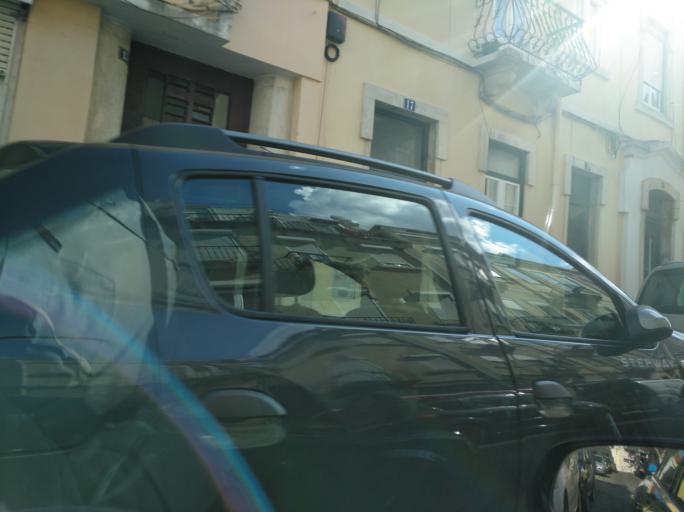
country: PT
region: Lisbon
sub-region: Lisbon
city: Lisbon
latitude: 38.7193
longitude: -9.1215
